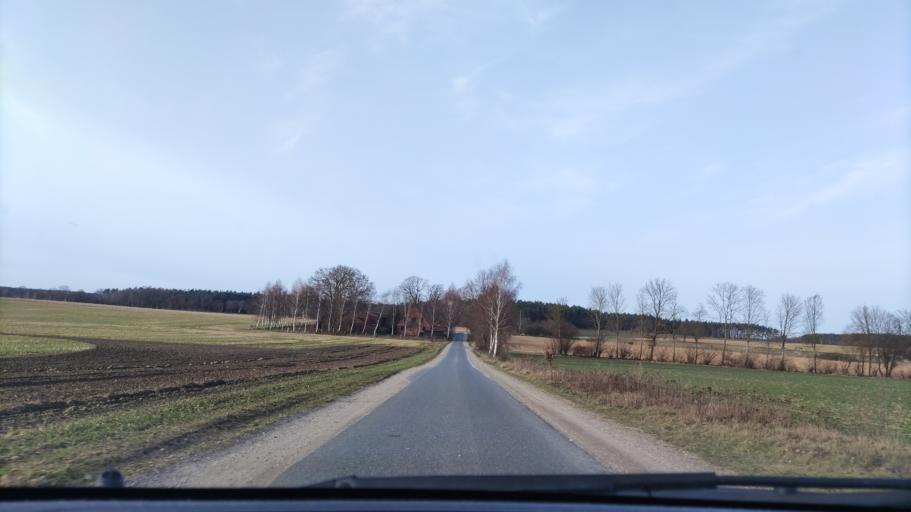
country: DE
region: Lower Saxony
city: Dahlenburg
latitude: 53.1922
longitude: 10.6973
